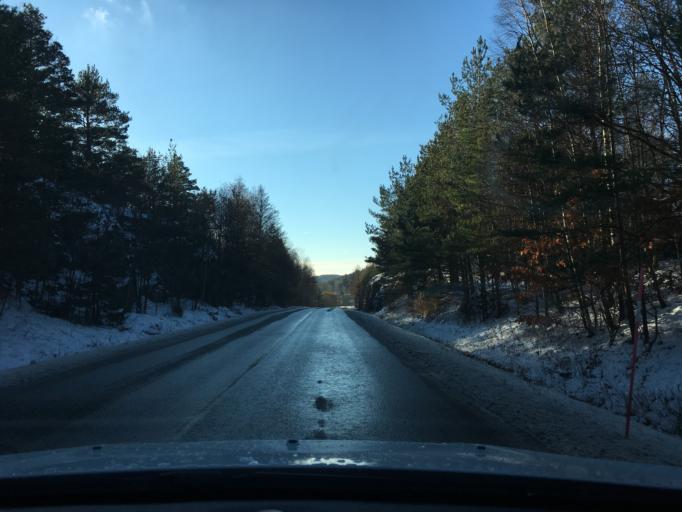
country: SE
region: Vaestra Goetaland
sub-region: Tjorns Kommun
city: Myggenas
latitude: 58.1345
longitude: 11.7578
